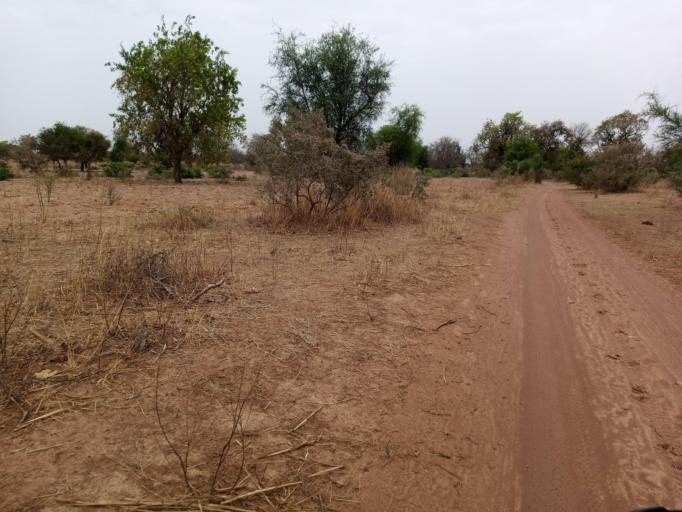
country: BF
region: Boucle du Mouhoun
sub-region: Province de la Kossi
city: Nouna
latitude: 12.8420
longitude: -4.0770
